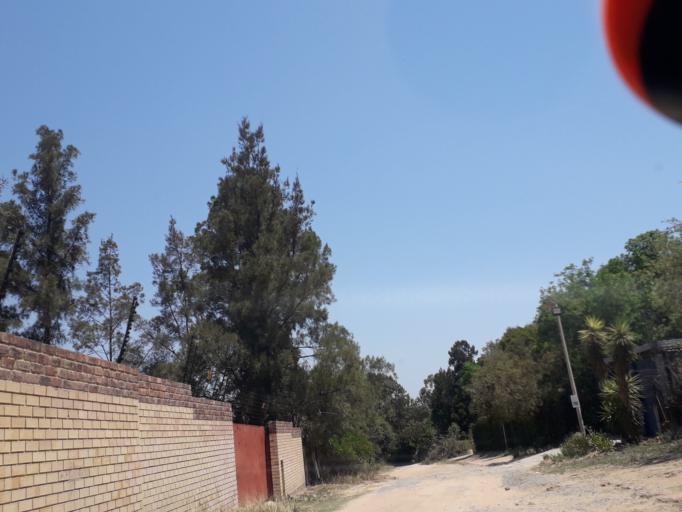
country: ZA
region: Gauteng
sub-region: City of Johannesburg Metropolitan Municipality
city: Midrand
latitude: -26.0206
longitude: 28.1313
